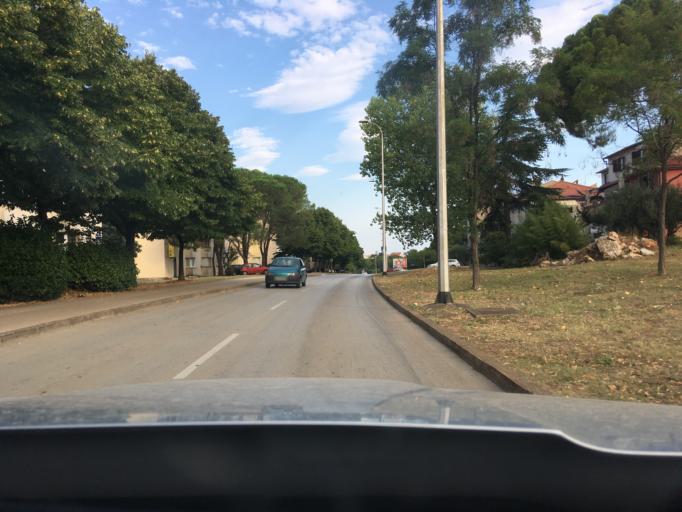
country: HR
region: Zadarska
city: Zadar
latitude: 44.1241
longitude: 15.2312
